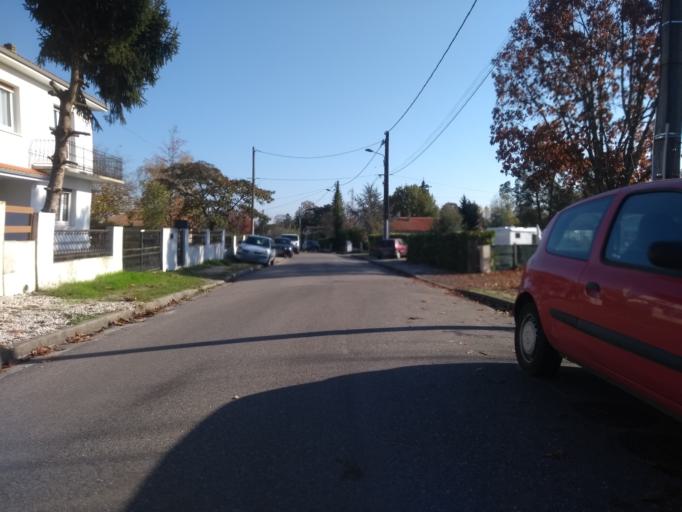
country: FR
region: Aquitaine
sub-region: Departement de la Gironde
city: Leognan
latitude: 44.7408
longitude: -0.6028
